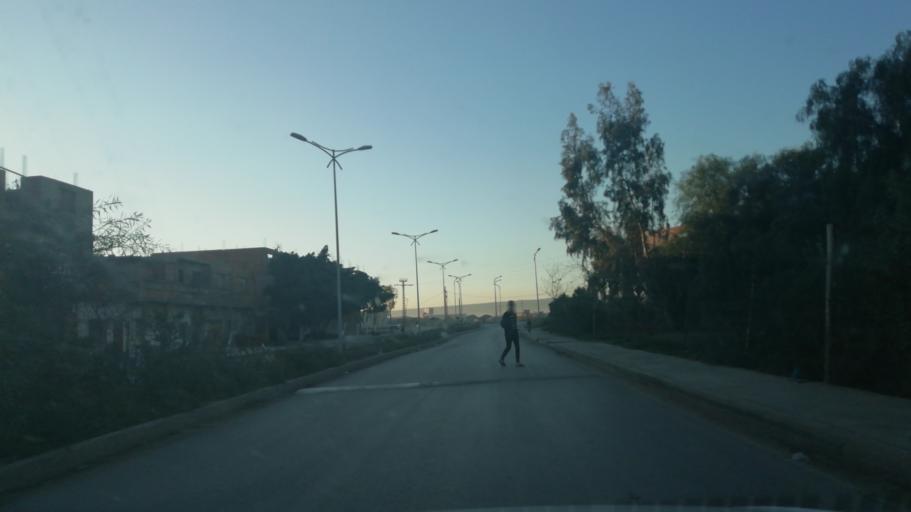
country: DZ
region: Oran
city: Es Senia
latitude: 35.6509
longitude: -0.5785
